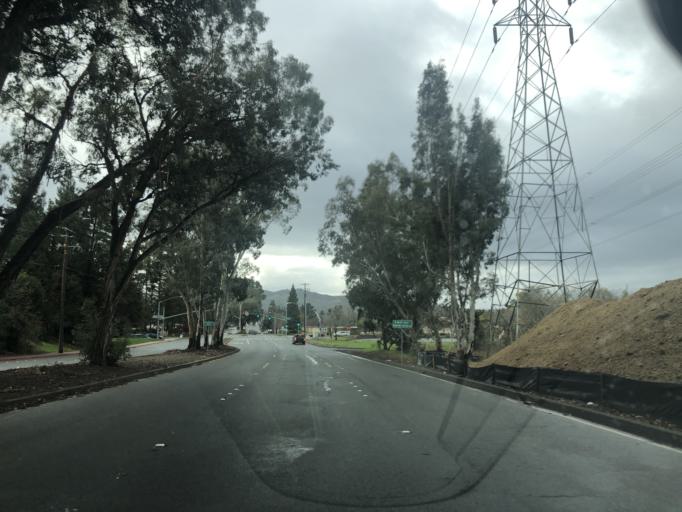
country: US
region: California
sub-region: Contra Costa County
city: Clayton
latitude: 37.9578
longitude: -121.9500
